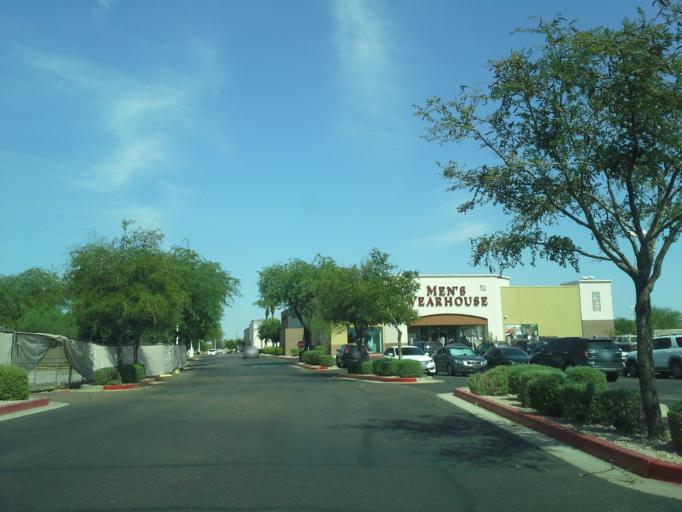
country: US
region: Arizona
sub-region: Maricopa County
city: Guadalupe
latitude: 33.3188
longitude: -111.9779
